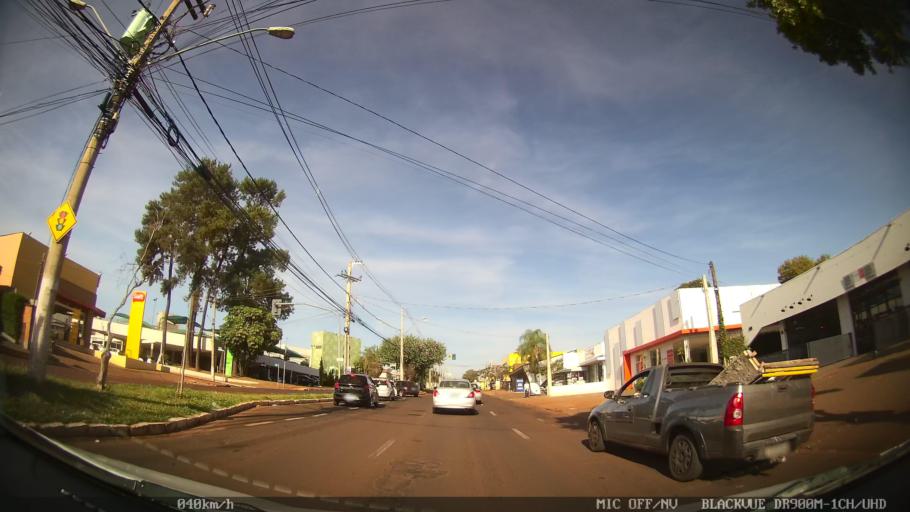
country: BR
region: Sao Paulo
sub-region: Ribeirao Preto
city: Ribeirao Preto
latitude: -21.1913
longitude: -47.8098
